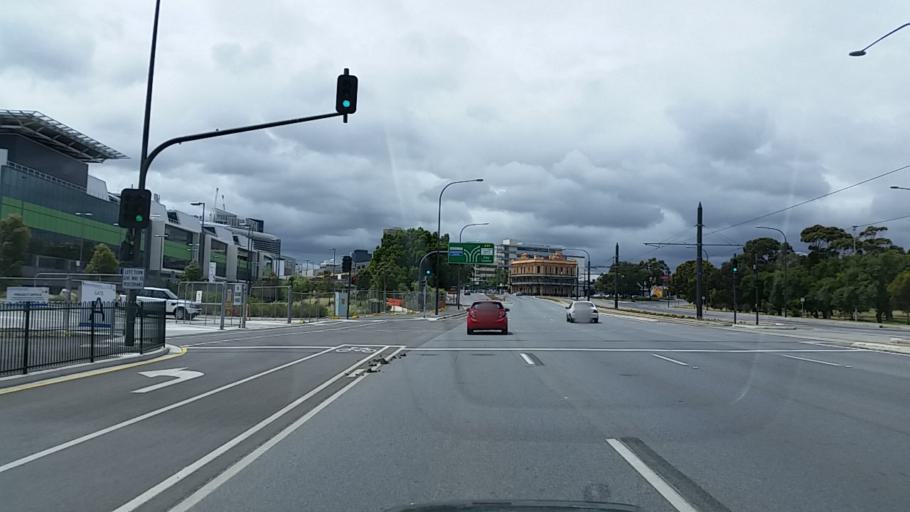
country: AU
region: South Australia
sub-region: Adelaide
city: North Adelaide
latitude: -34.9210
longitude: 138.5847
